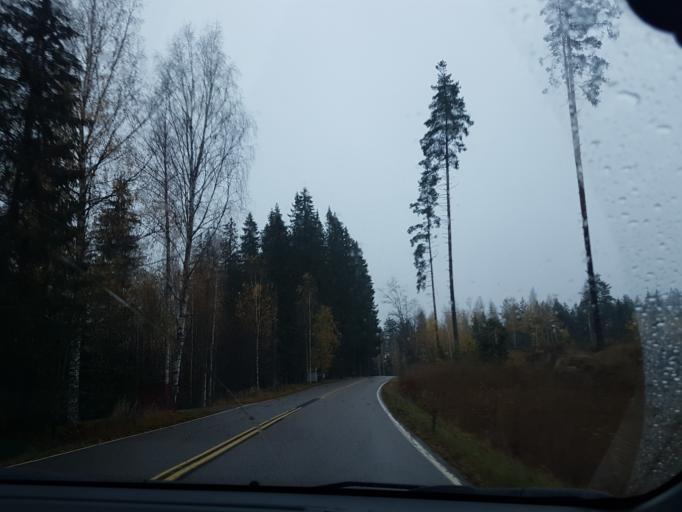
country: FI
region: Uusimaa
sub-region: Helsinki
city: Maentsaelae
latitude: 60.6094
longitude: 25.2086
